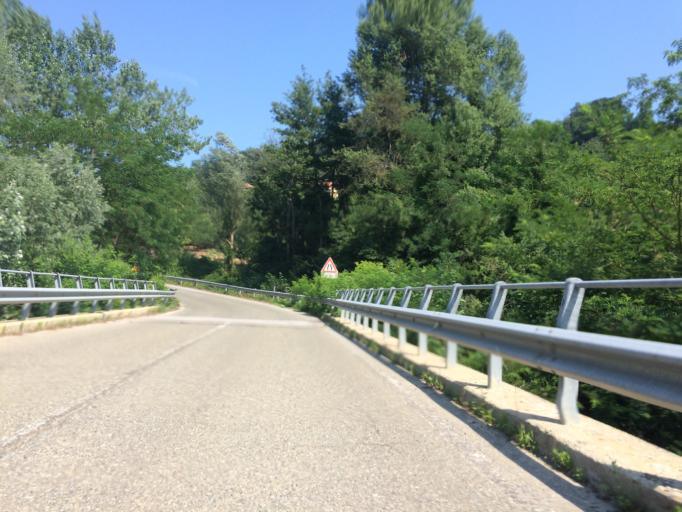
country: IT
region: Piedmont
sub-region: Provincia di Cuneo
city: Arguello
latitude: 44.5779
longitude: 8.1149
